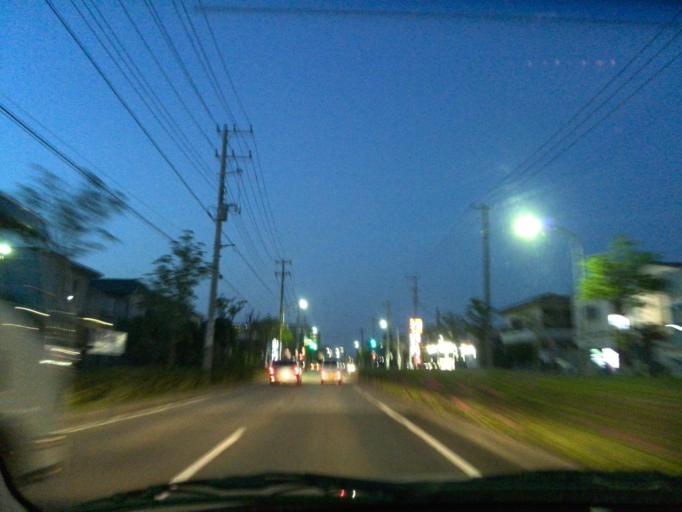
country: JP
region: Chiba
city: Funabashi
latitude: 35.6731
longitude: 140.0106
